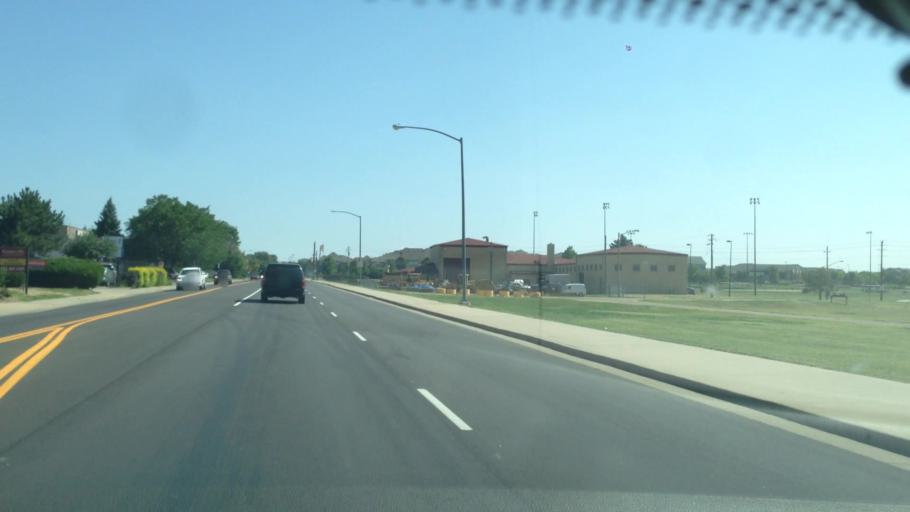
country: US
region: Colorado
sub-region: Adams County
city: Aurora
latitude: 39.7290
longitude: -104.8754
